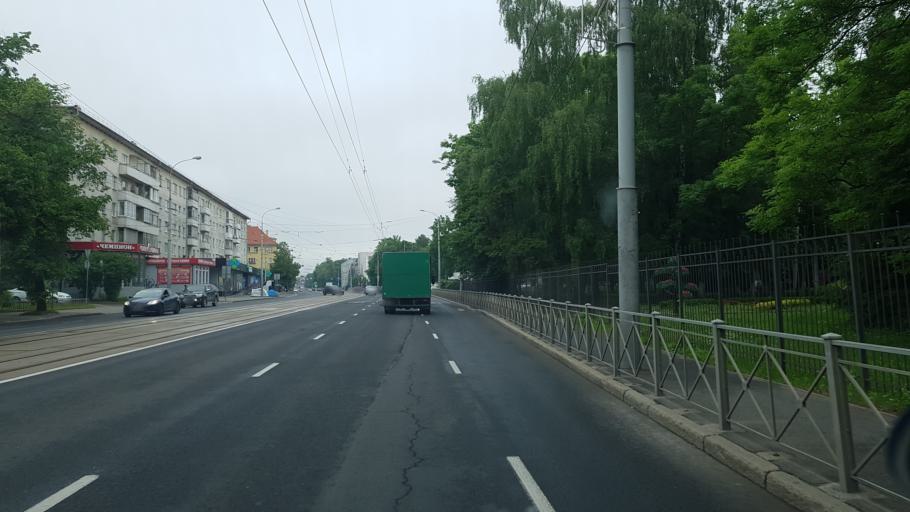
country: RU
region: Kaliningrad
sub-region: Gorod Kaliningrad
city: Kaliningrad
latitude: 54.7283
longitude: 20.4930
